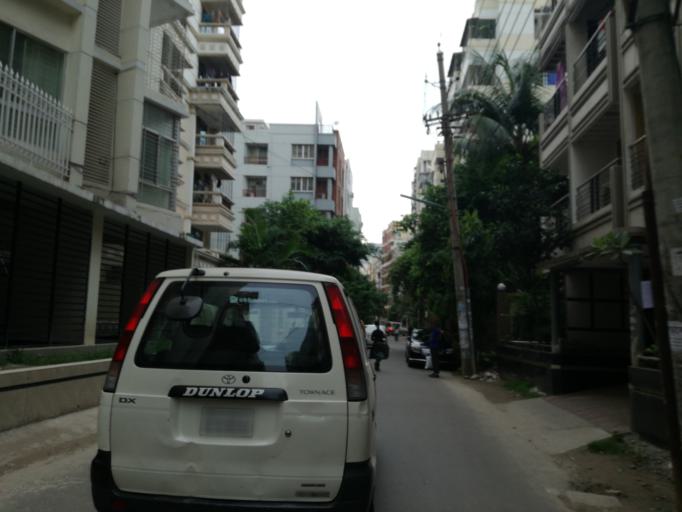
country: BD
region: Dhaka
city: Paltan
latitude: 23.7737
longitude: 90.4131
